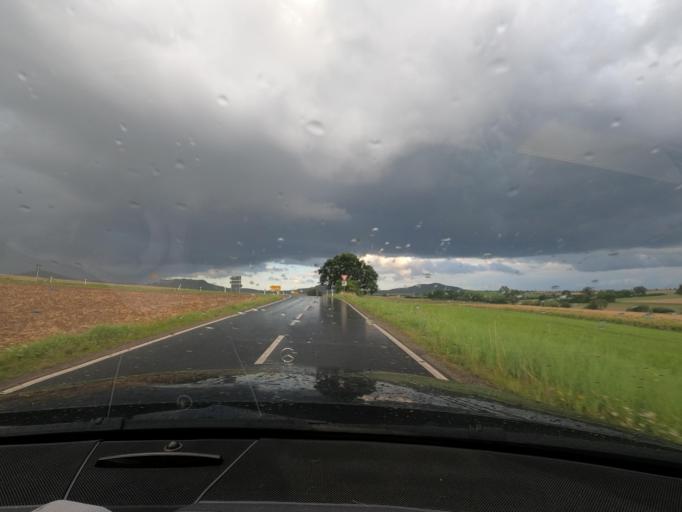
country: DE
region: Hesse
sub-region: Regierungsbezirk Kassel
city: Wolfhagen
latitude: 51.3272
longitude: 9.2339
